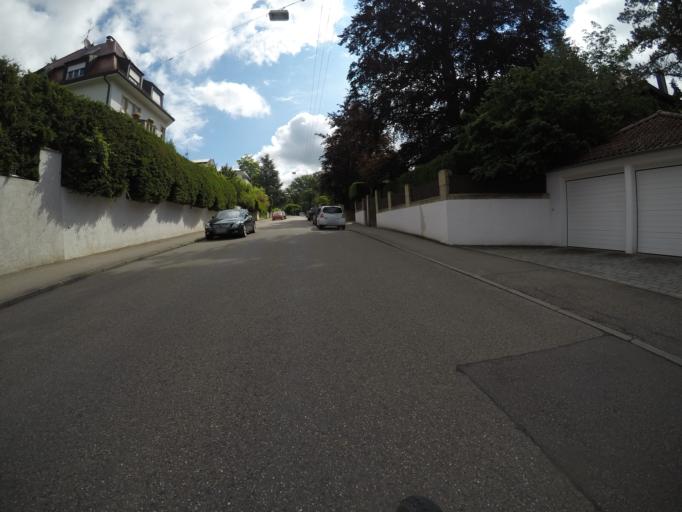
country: DE
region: Baden-Wuerttemberg
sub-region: Regierungsbezirk Stuttgart
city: Stuttgart
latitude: 48.7488
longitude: 9.1800
